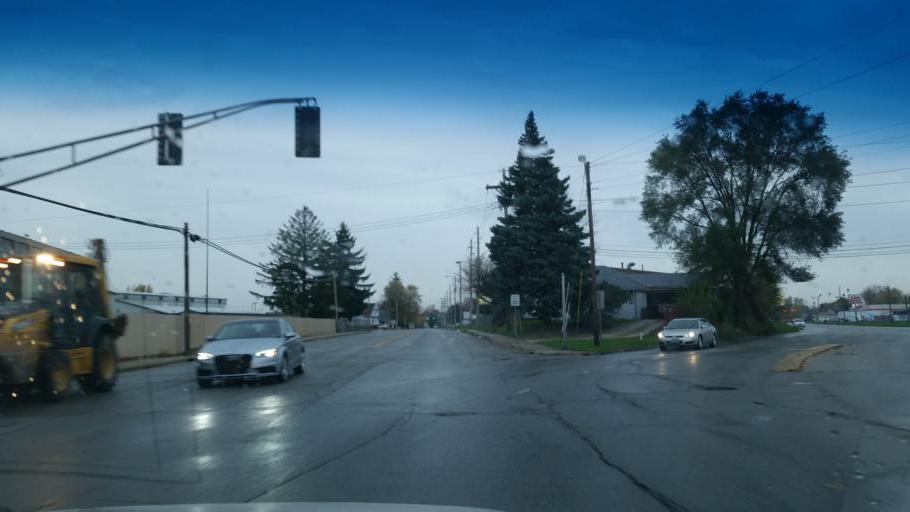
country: US
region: Indiana
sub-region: Howard County
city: Kokomo
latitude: 40.4731
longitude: -86.1275
